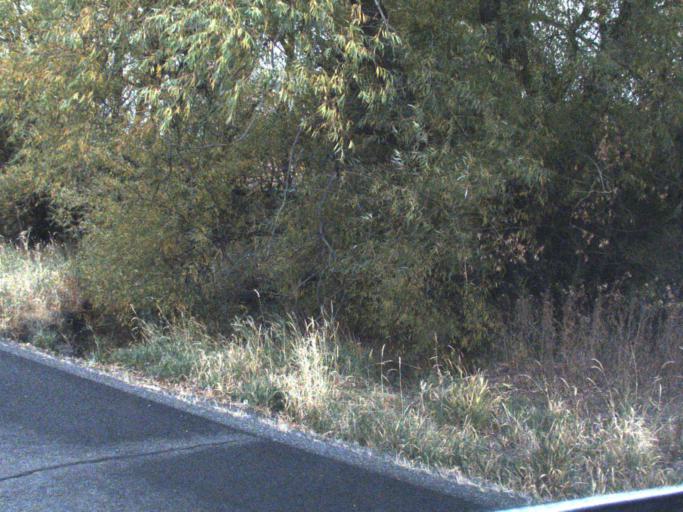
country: US
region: Washington
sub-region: Whitman County
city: Pullman
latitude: 46.7035
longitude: -117.2042
